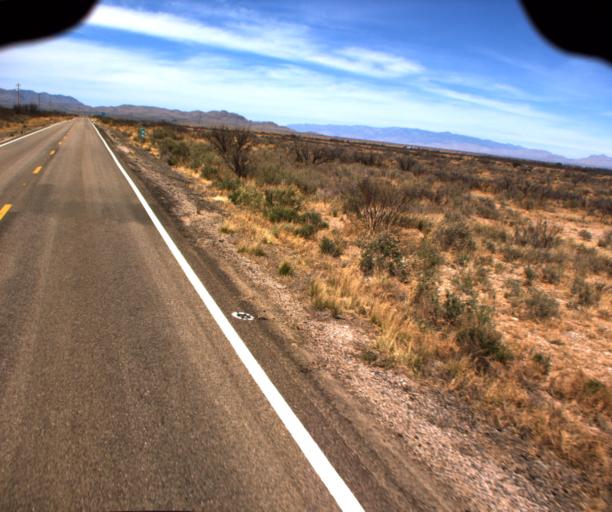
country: US
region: Arizona
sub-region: Cochise County
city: Willcox
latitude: 32.1647
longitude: -109.9435
